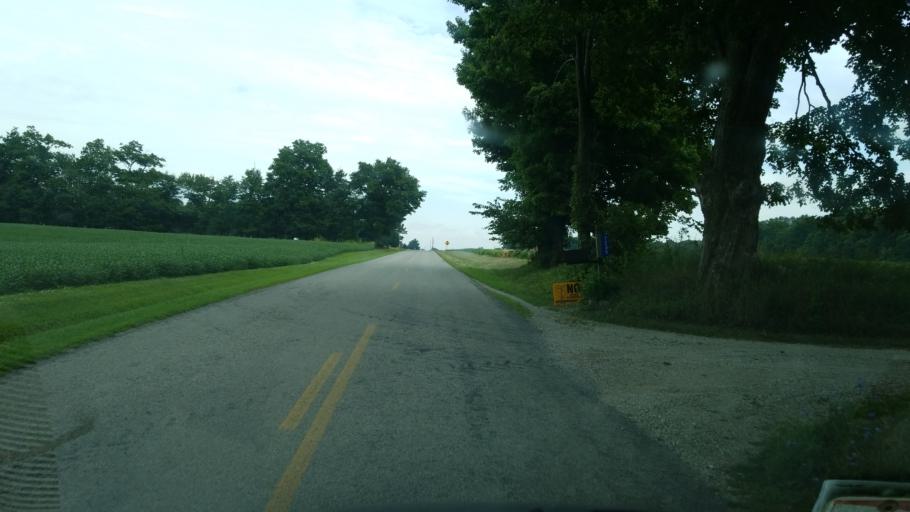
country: US
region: Ohio
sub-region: Seneca County
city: Tiffin
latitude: 41.0191
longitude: -83.0546
